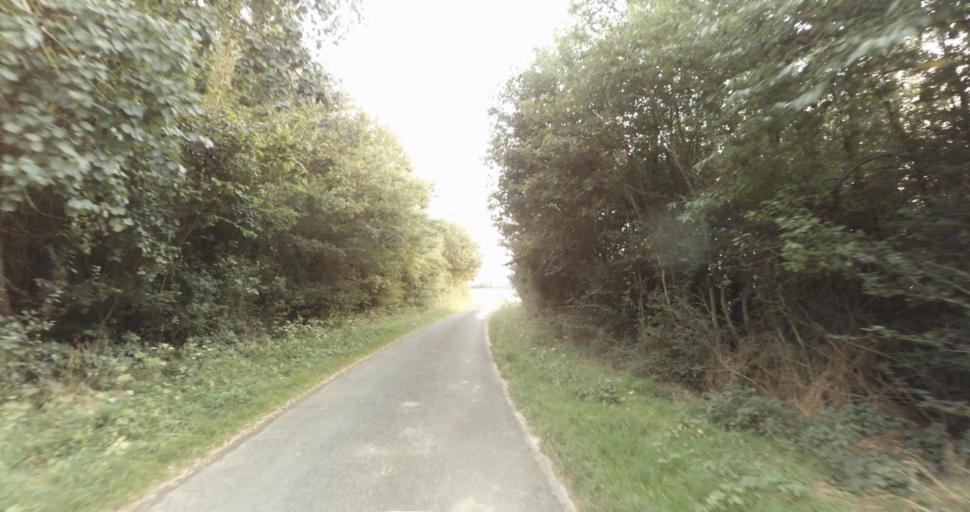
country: FR
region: Haute-Normandie
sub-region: Departement de l'Eure
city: La Madeleine-de-Nonancourt
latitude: 48.8604
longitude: 1.2217
